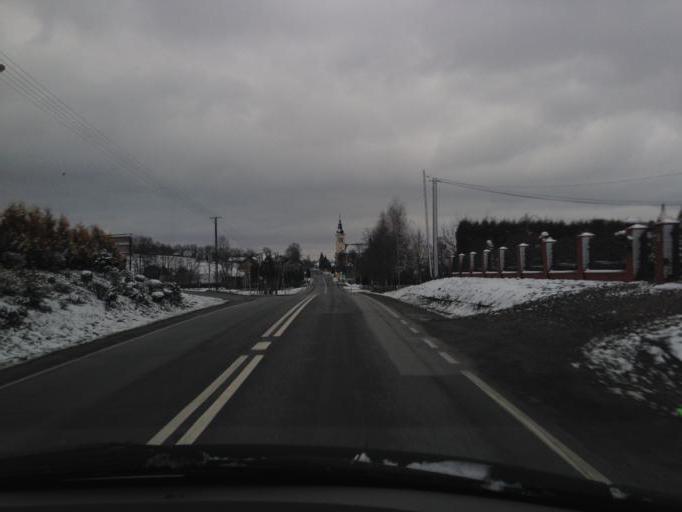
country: PL
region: Lesser Poland Voivodeship
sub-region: Powiat tarnowski
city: Siemiechow
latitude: 49.8538
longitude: 20.8943
